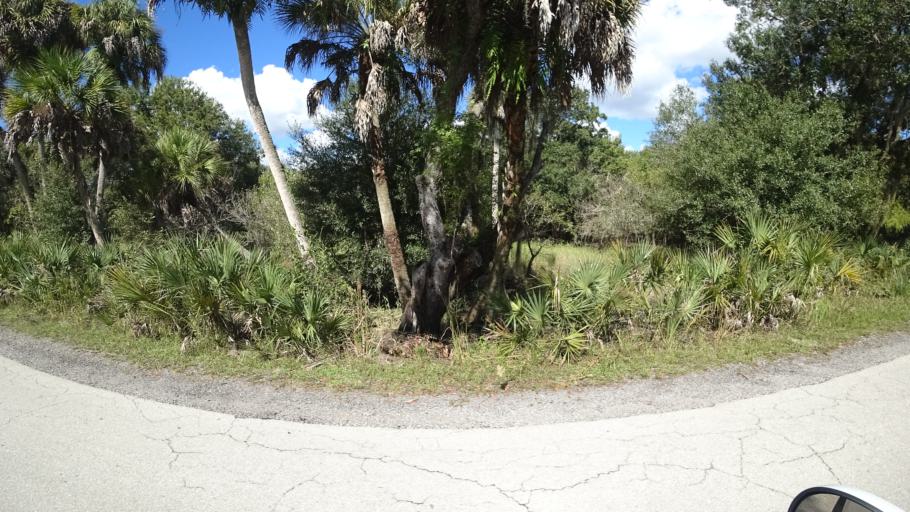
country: US
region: Florida
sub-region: Sarasota County
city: Lake Sarasota
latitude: 27.2742
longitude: -82.2676
